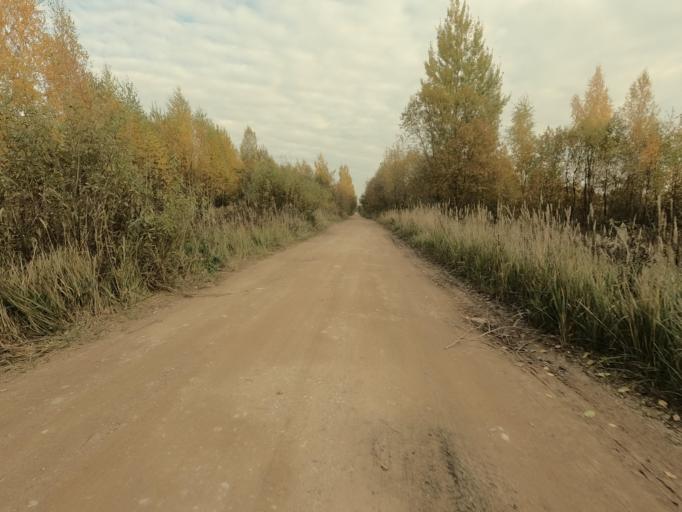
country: RU
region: Novgorod
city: Pankovka
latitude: 58.8977
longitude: 30.9968
